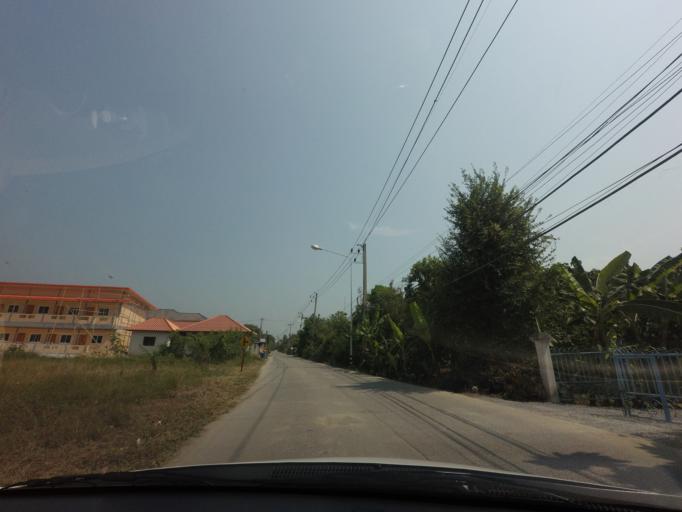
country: TH
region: Nakhon Pathom
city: Sam Phran
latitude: 13.7483
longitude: 100.2626
